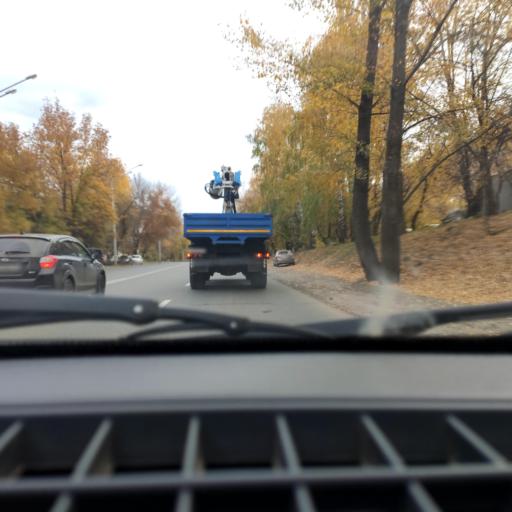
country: RU
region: Bashkortostan
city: Avdon
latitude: 54.6827
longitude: 55.8101
